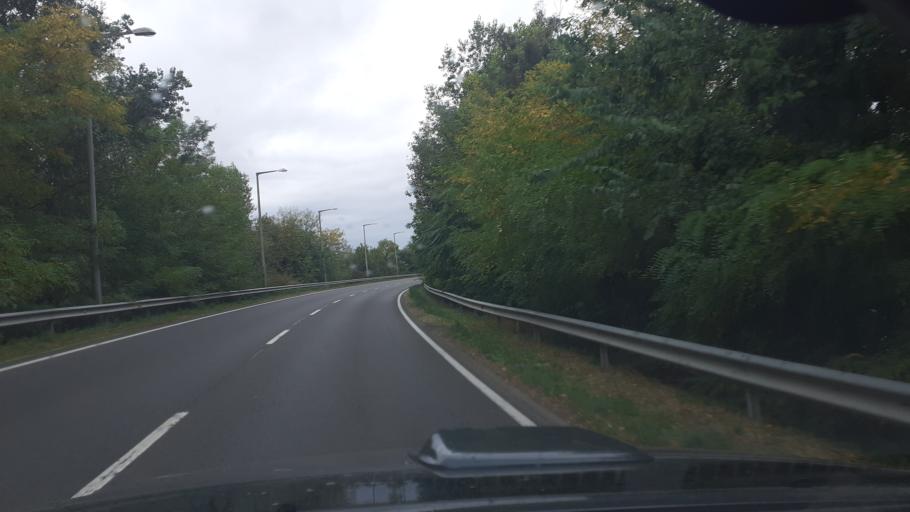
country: HU
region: Tolna
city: Dunafoldvar
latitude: 46.7937
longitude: 18.9264
